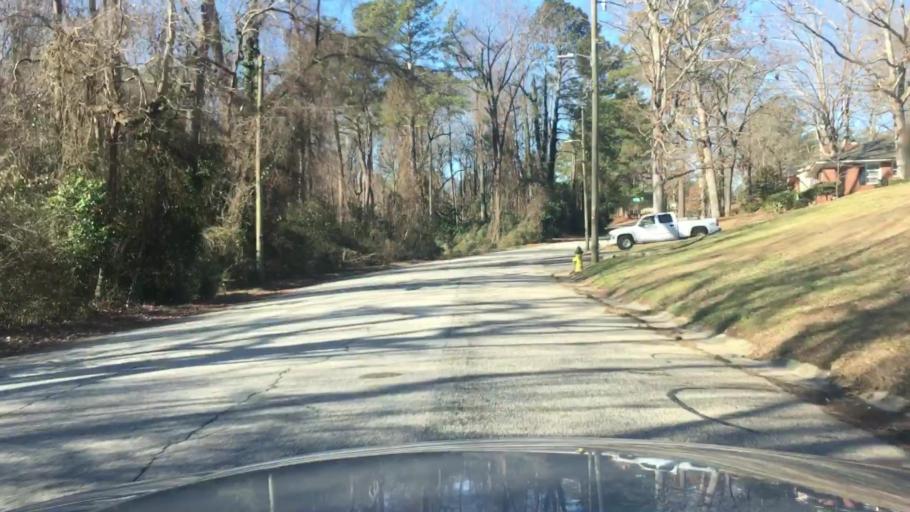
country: US
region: North Carolina
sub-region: Cumberland County
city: Fayetteville
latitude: 35.0766
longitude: -78.9188
